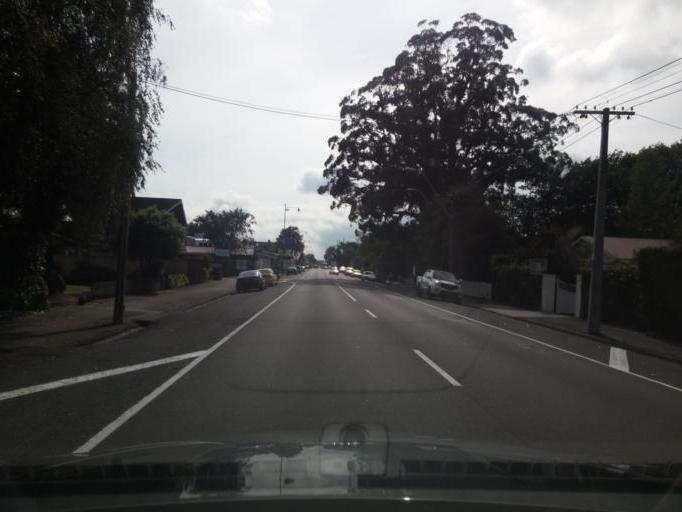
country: NZ
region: Wellington
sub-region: Masterton District
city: Masterton
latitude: -41.0832
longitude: 175.4572
